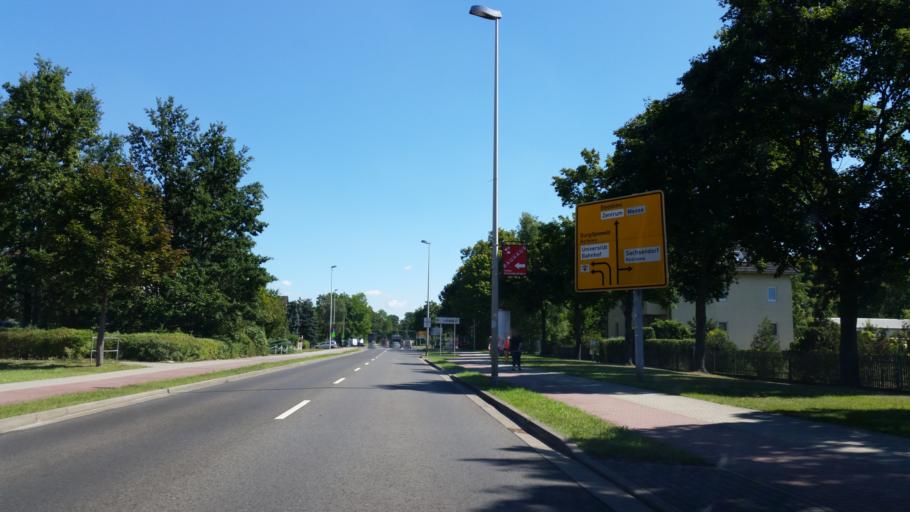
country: DE
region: Brandenburg
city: Cottbus
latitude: 51.7356
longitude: 14.3209
